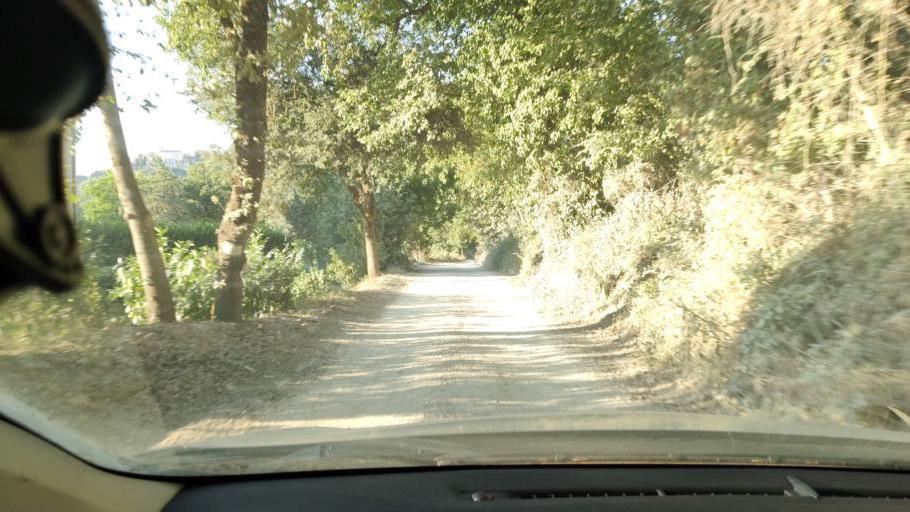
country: IT
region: Umbria
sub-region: Provincia di Terni
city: Amelia
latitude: 42.5485
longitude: 12.4100
